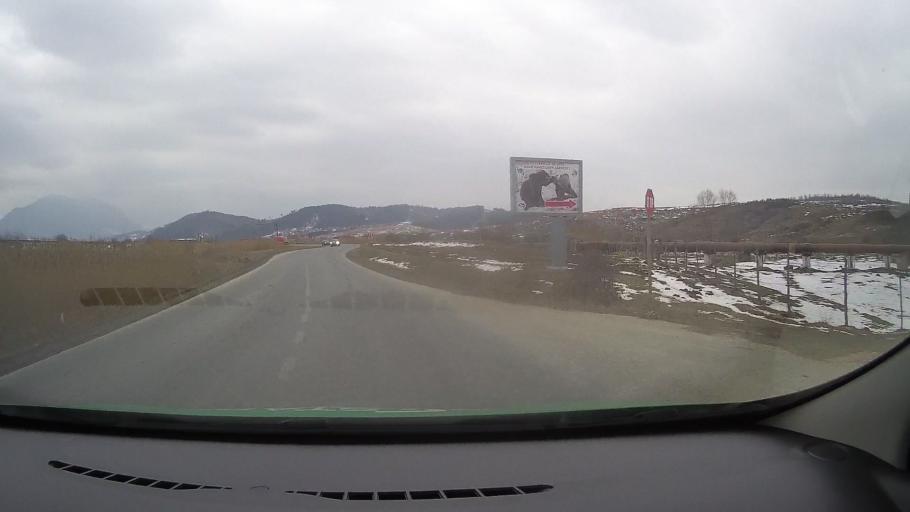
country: RO
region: Brasov
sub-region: Comuna Zarnesti
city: Tohanu Nou
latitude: 45.5780
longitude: 25.3886
